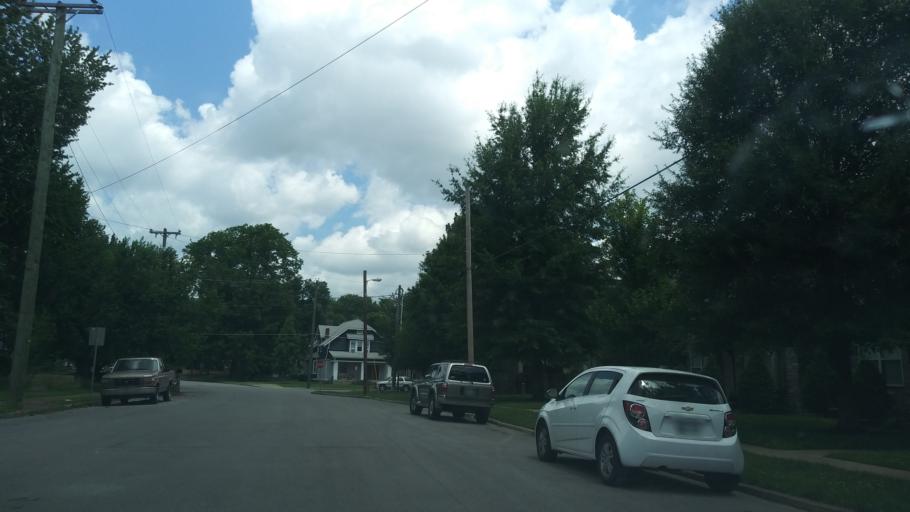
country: US
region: Tennessee
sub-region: Davidson County
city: Nashville
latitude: 36.1304
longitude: -86.7805
